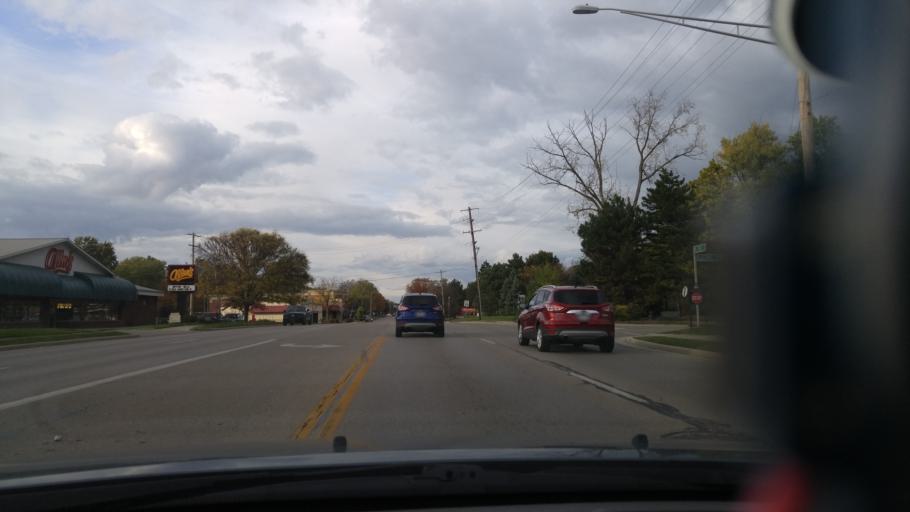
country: US
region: Ohio
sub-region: Franklin County
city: Westerville
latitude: 40.1149
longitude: -82.9275
